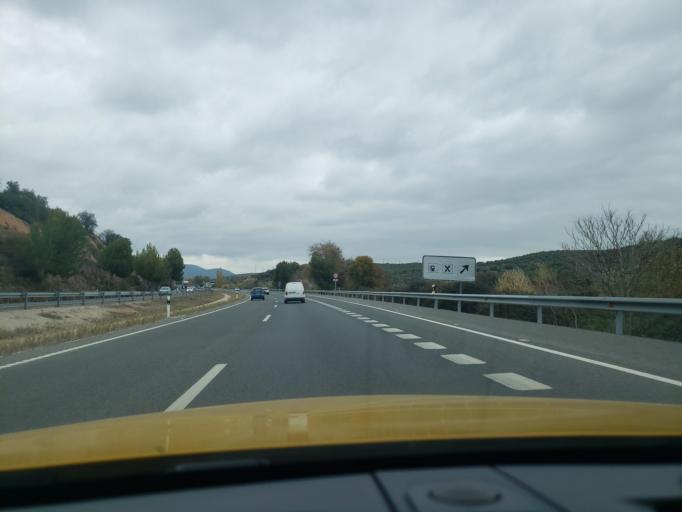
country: ES
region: Andalusia
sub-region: Provincia de Granada
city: Deifontes
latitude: 37.3392
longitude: -3.6226
